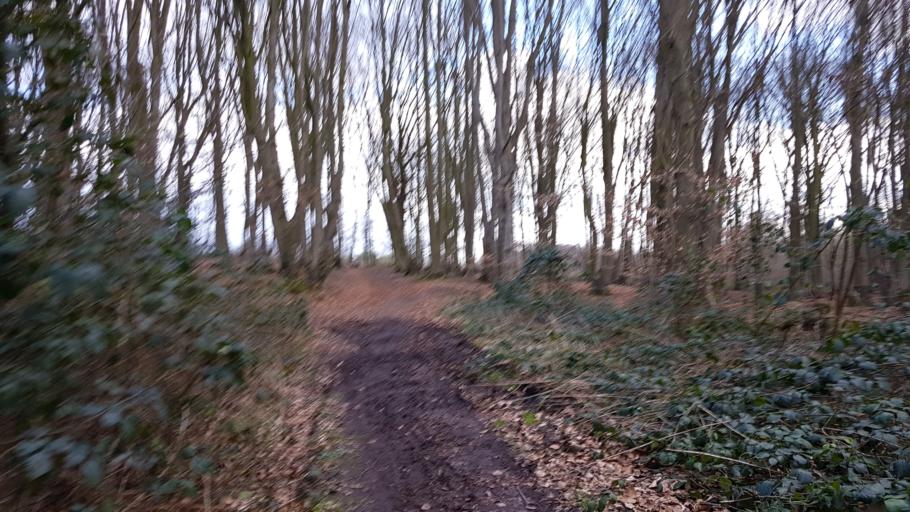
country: DE
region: North Rhine-Westphalia
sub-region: Regierungsbezirk Dusseldorf
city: Bruggen
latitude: 51.2351
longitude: 6.2174
